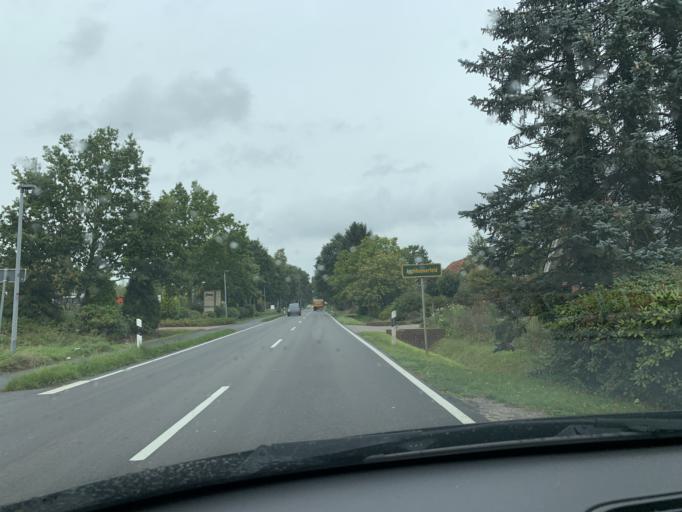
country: DE
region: Lower Saxony
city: Bad Zwischenahn
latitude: 53.1772
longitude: 8.0694
